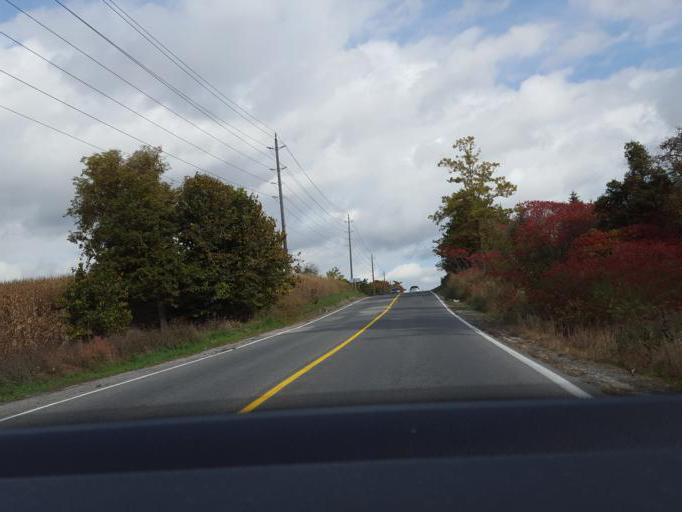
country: CA
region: Ontario
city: Markham
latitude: 43.8426
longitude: -79.2254
